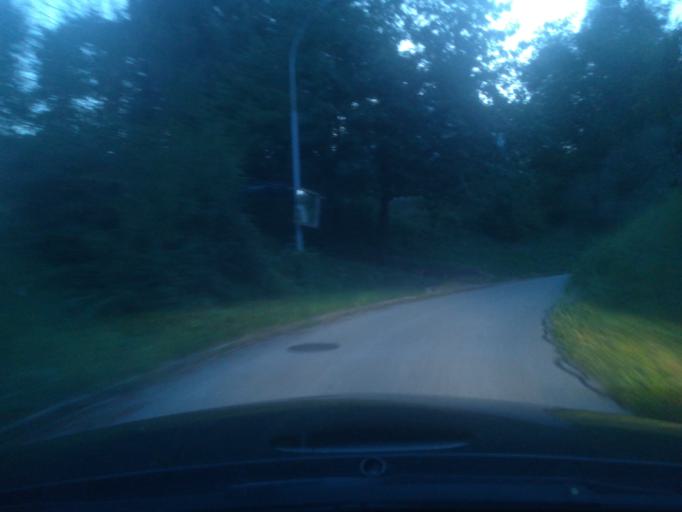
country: AT
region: Upper Austria
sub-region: Wels-Land
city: Thalheim bei Wels
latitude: 48.1504
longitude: 14.0742
